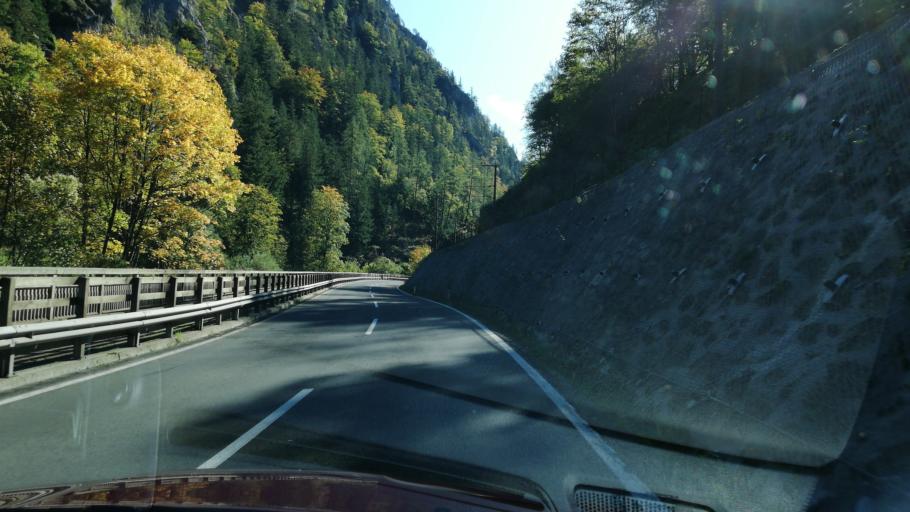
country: AT
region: Styria
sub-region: Politischer Bezirk Leoben
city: Eisenerz
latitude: 47.5823
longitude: 14.8235
